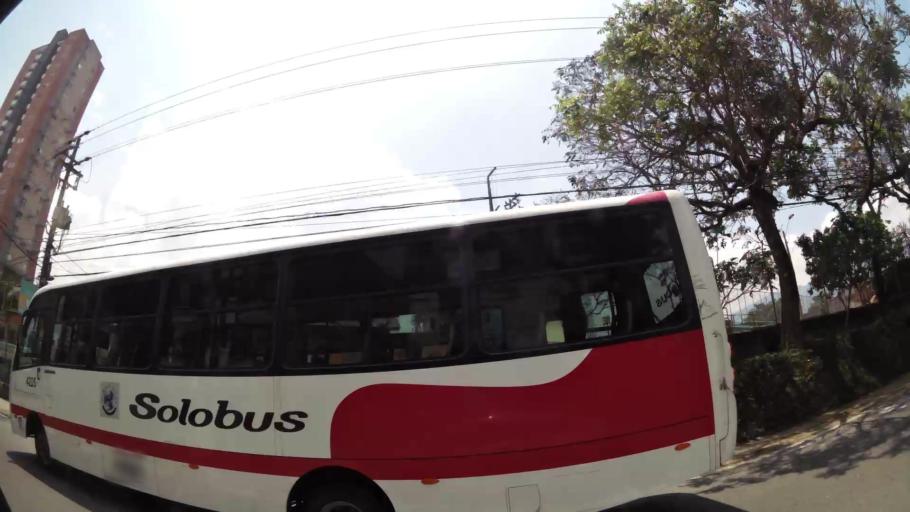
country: CO
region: Antioquia
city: Sabaneta
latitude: 6.1687
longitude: -75.6170
